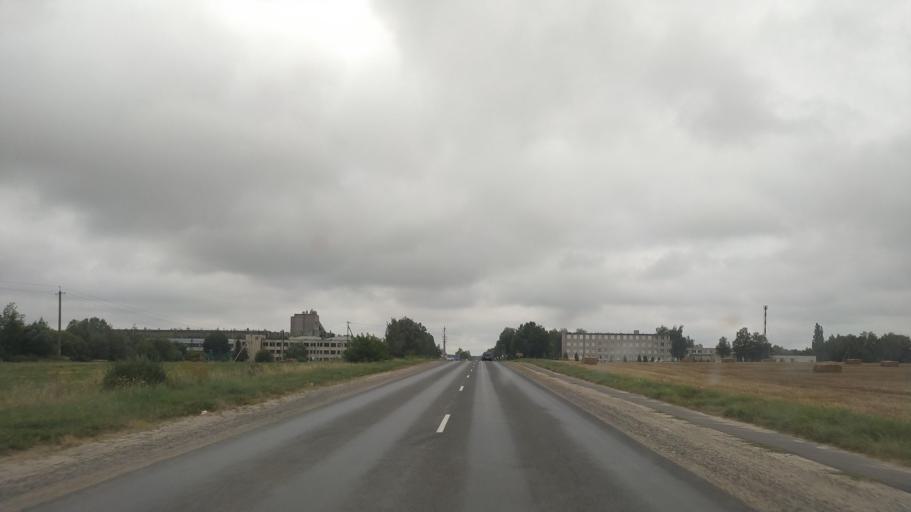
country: BY
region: Brest
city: Byaroza
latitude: 52.5497
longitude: 24.9431
